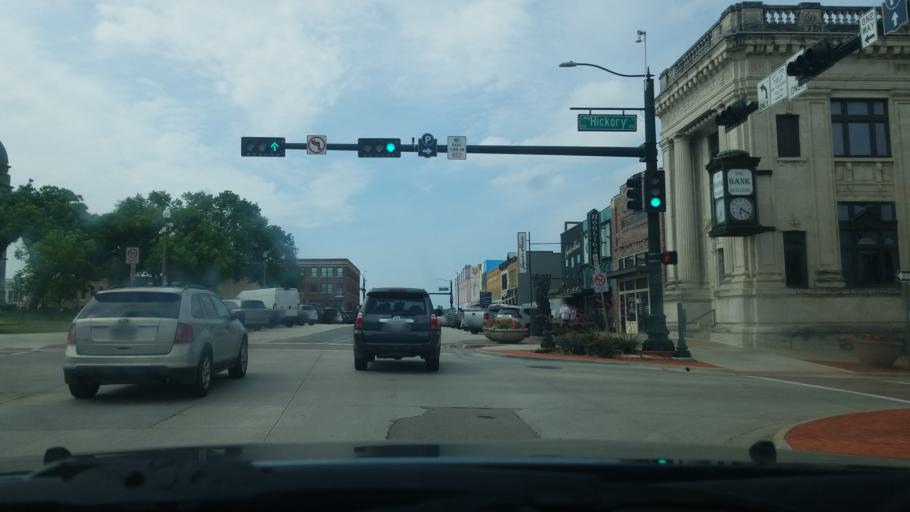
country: US
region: Texas
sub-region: Denton County
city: Denton
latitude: 33.2144
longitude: -97.1324
